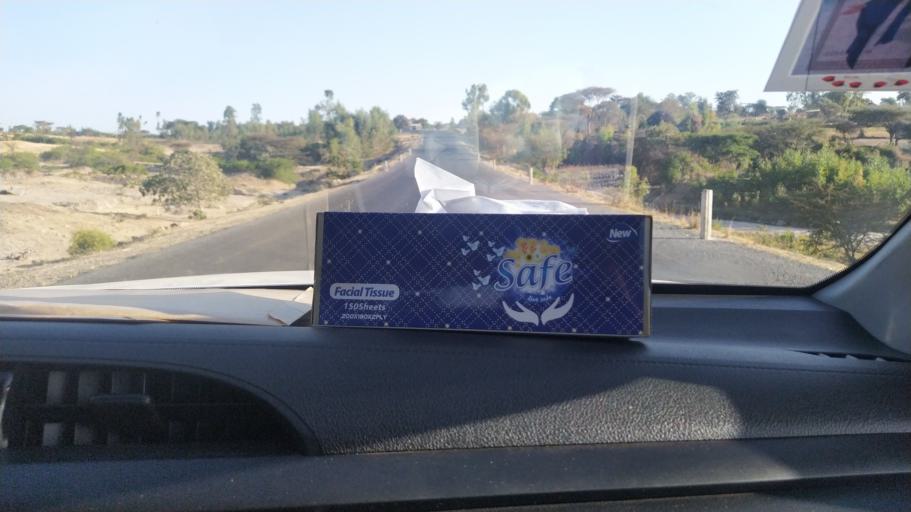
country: ET
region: Southern Nations, Nationalities, and People's Region
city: K'olito
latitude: 7.7012
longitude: 38.1304
